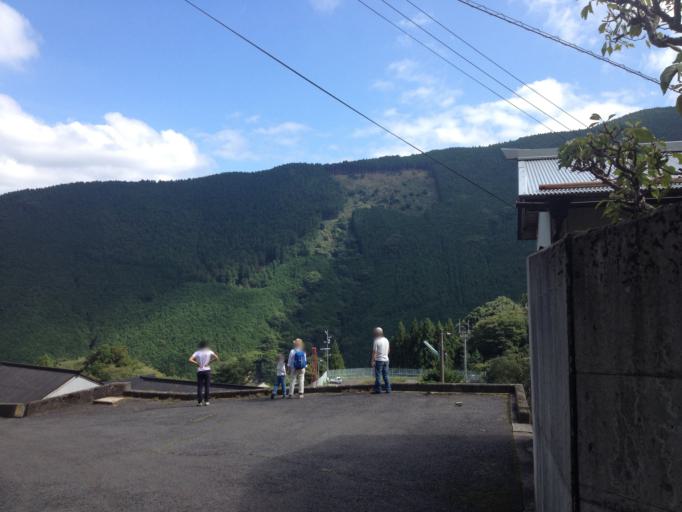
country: JP
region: Nara
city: Yoshino-cho
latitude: 34.3240
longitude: 135.9481
